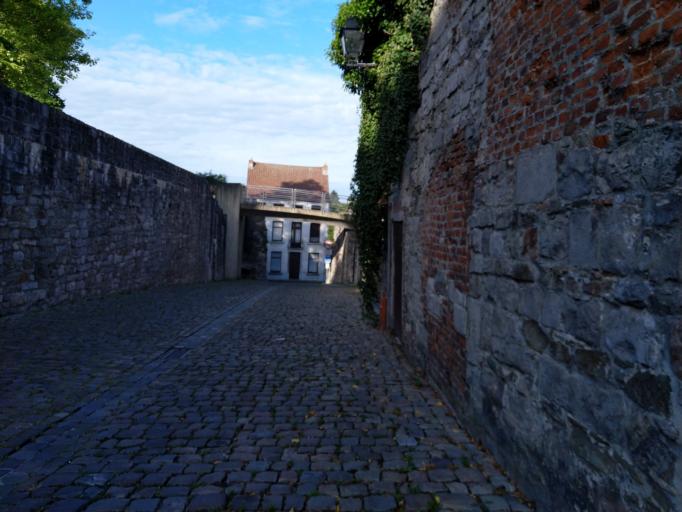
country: BE
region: Wallonia
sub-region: Province du Hainaut
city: Binche
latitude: 50.4092
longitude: 4.1646
